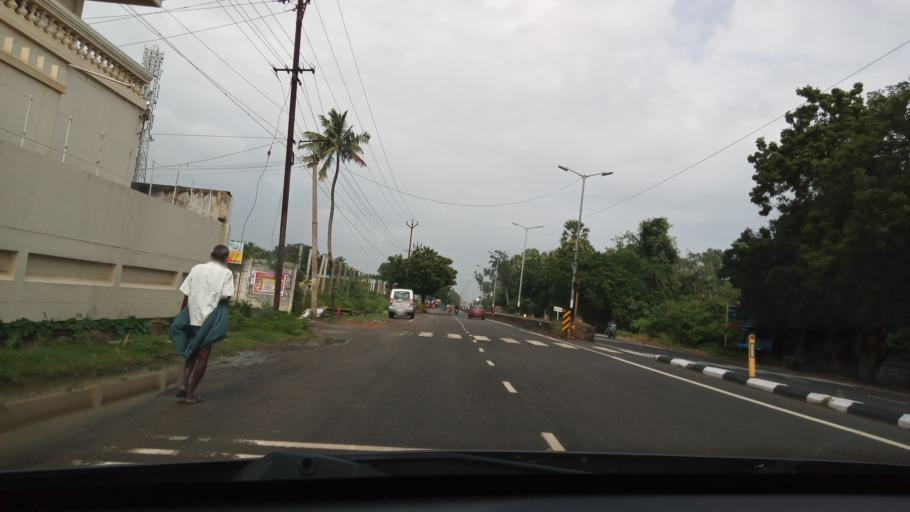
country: IN
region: Tamil Nadu
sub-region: Villupuram
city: Auroville
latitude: 12.0239
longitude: 79.8611
